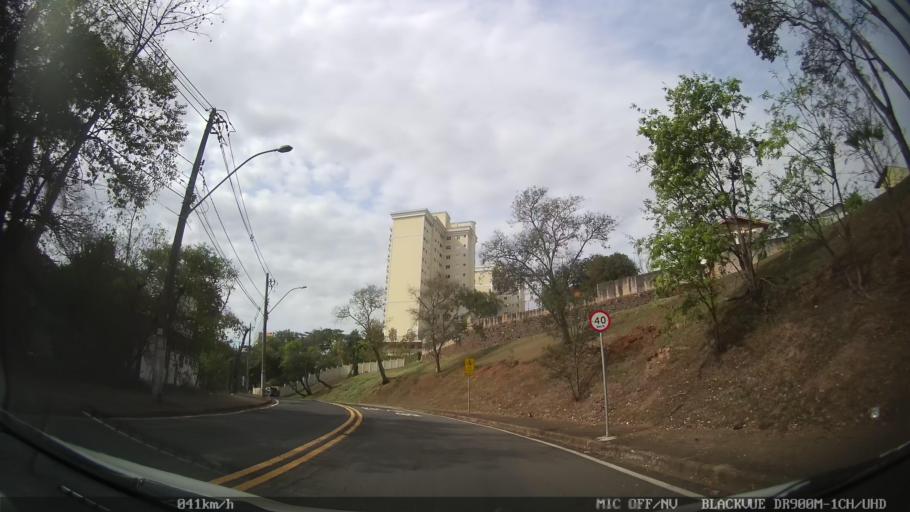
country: BR
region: Sao Paulo
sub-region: Piracicaba
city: Piracicaba
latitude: -22.7274
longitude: -47.6578
